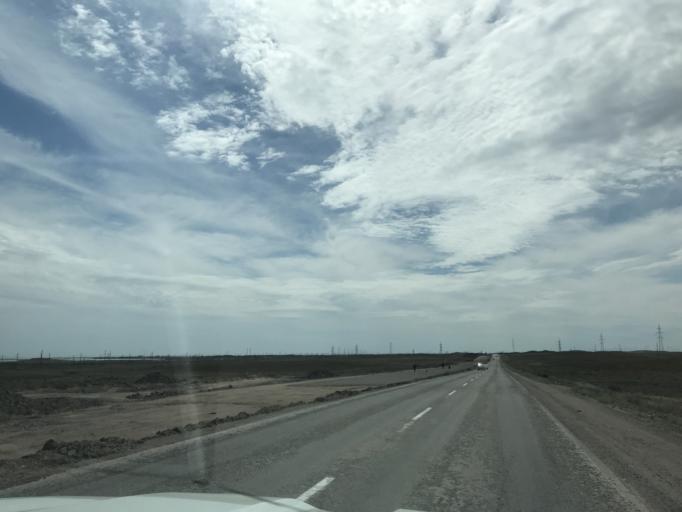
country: KZ
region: Almaty Oblysy
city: Ulken
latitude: 45.2206
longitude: 73.8600
